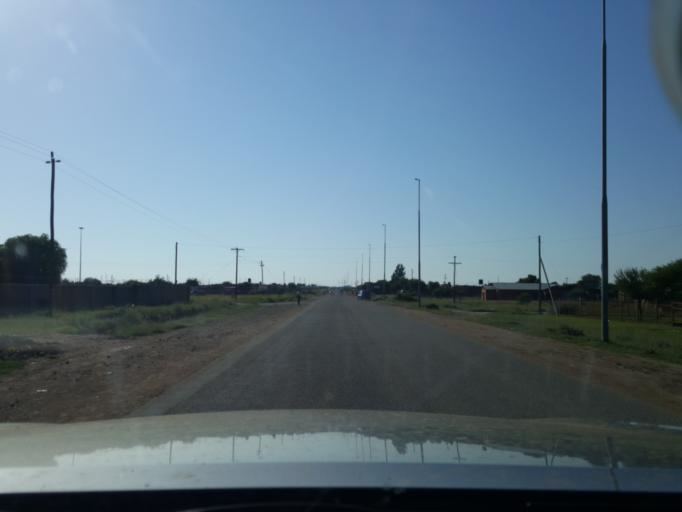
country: ZA
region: North-West
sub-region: Ngaka Modiri Molema District Municipality
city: Mmabatho
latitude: -25.8335
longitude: 25.6608
